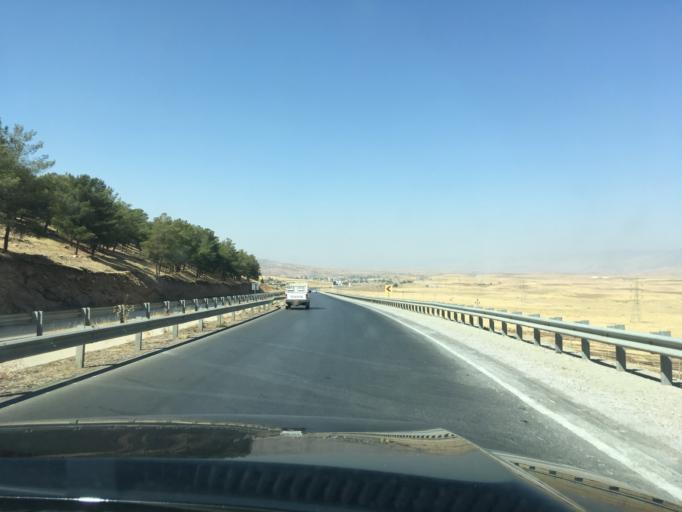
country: IQ
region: Arbil
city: Shaqlawah
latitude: 36.4895
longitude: 44.3787
